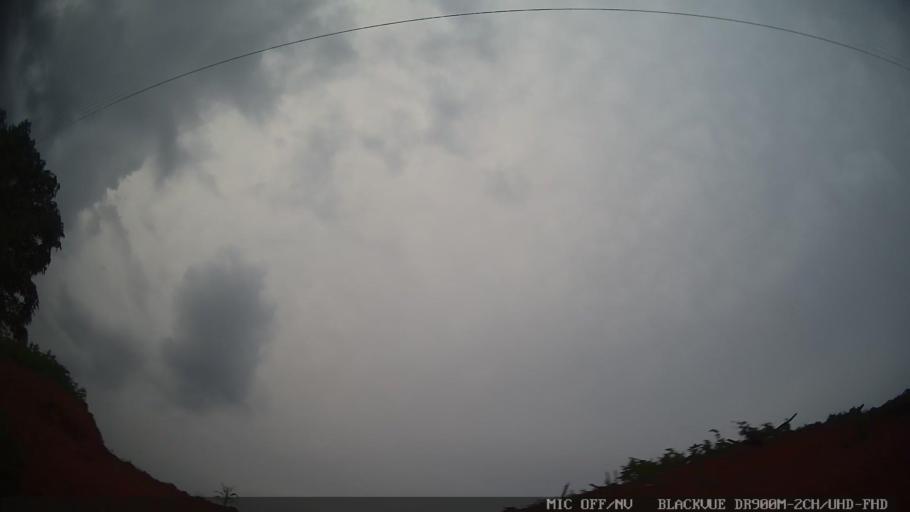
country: BR
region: Sao Paulo
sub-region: Braganca Paulista
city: Braganca Paulista
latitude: -22.9487
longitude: -46.5829
